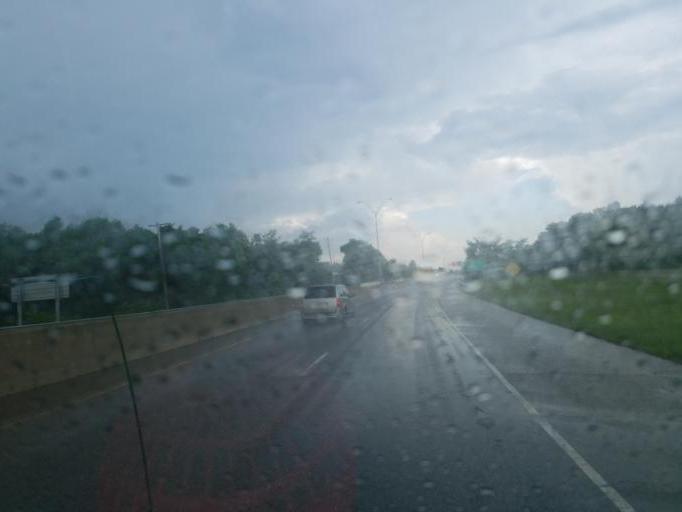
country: US
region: Ohio
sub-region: Summit County
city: Sawyerwood
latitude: 41.0250
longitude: -81.4760
